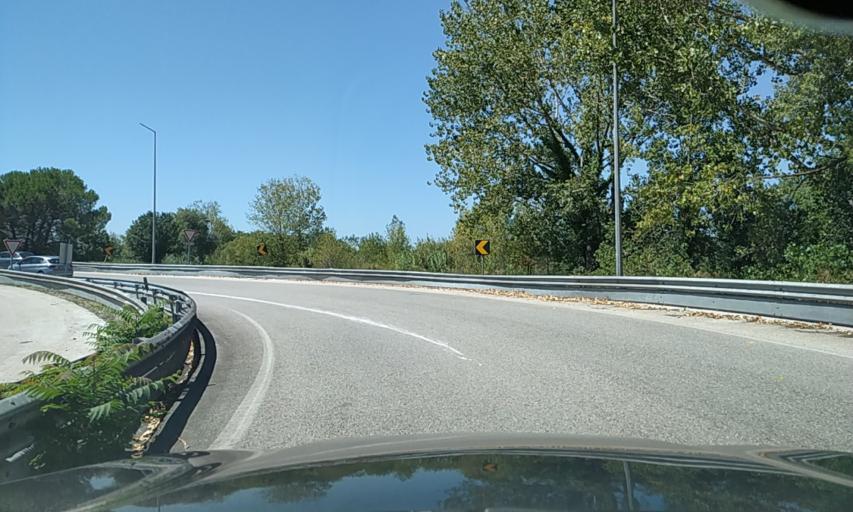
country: PT
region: Coimbra
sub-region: Coimbra
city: Coimbra
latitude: 40.2157
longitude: -8.4426
